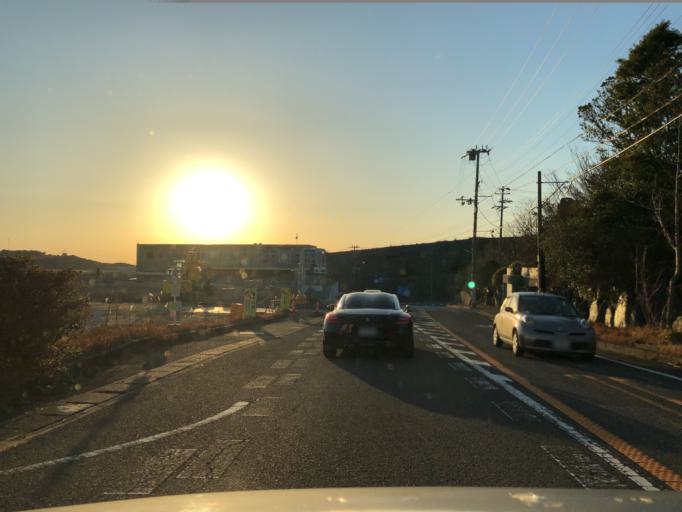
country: JP
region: Wakayama
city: Tanabe
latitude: 33.6693
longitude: 135.3639
